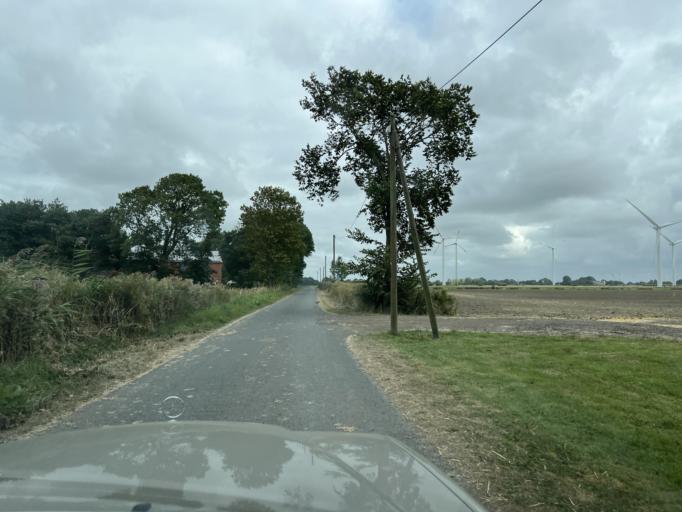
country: DE
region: Schleswig-Holstein
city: Groven
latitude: 54.2997
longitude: 8.9928
